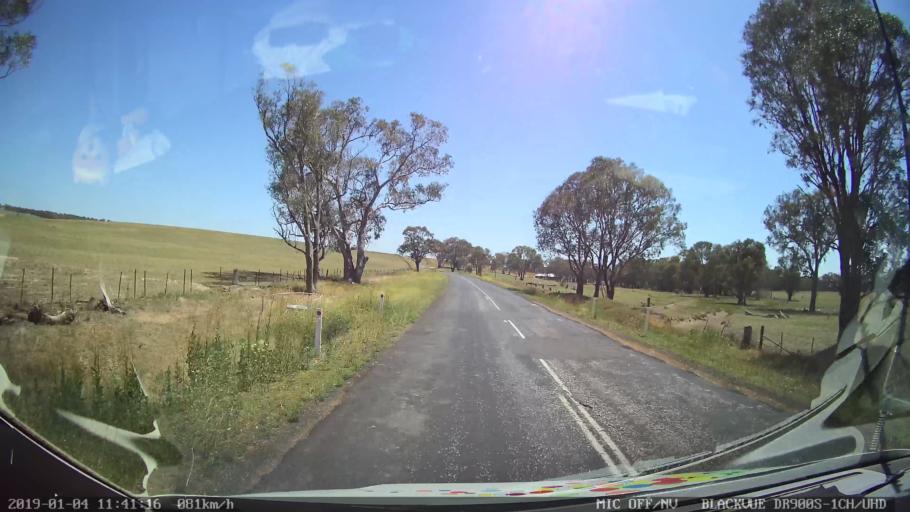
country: AU
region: New South Wales
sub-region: Cabonne
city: Molong
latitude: -32.9957
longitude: 148.7872
